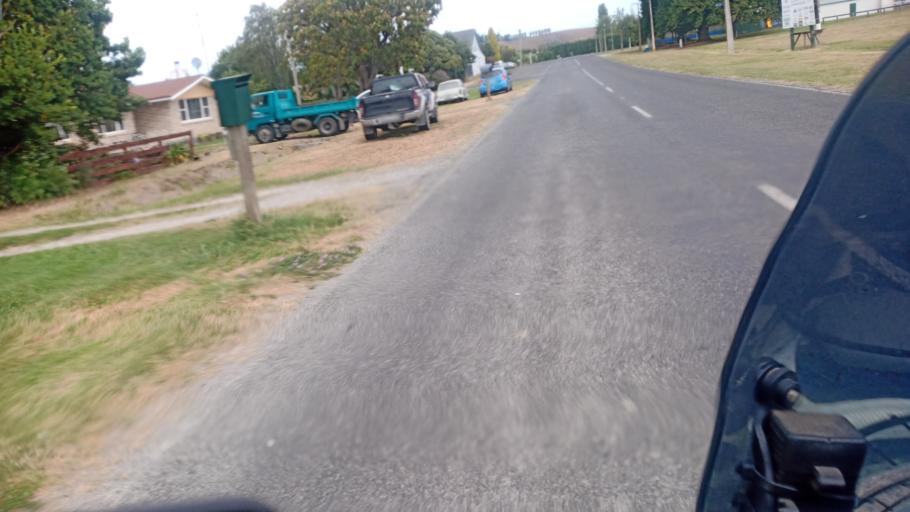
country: NZ
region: Gisborne
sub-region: Gisborne District
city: Gisborne
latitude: -38.6231
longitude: 177.8903
